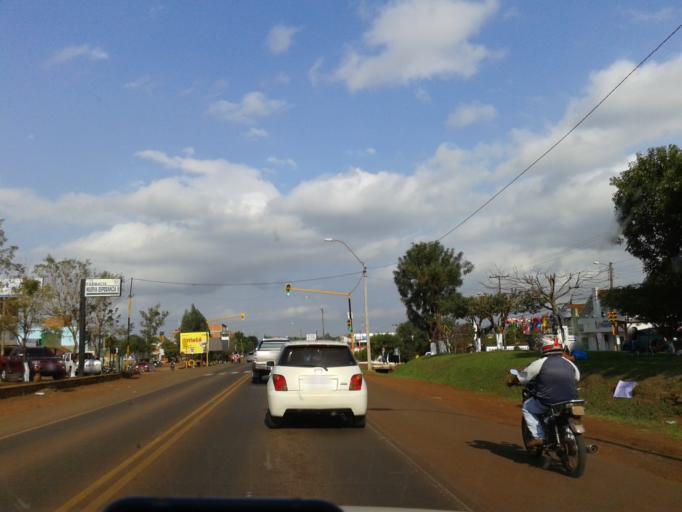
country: PY
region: Itapua
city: Arquitecto Tomas Romero Pereira
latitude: -26.5286
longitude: -55.2613
